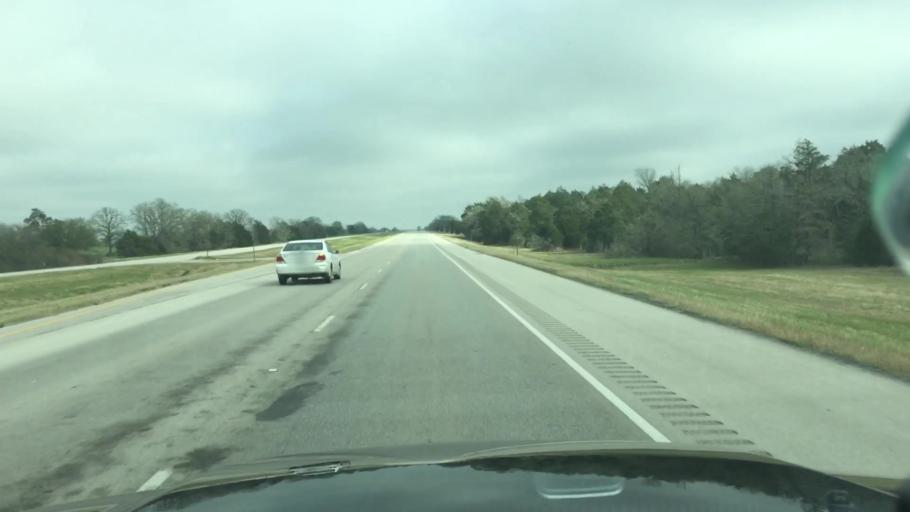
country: US
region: Texas
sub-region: Lee County
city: Giddings
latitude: 30.1440
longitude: -96.7324
